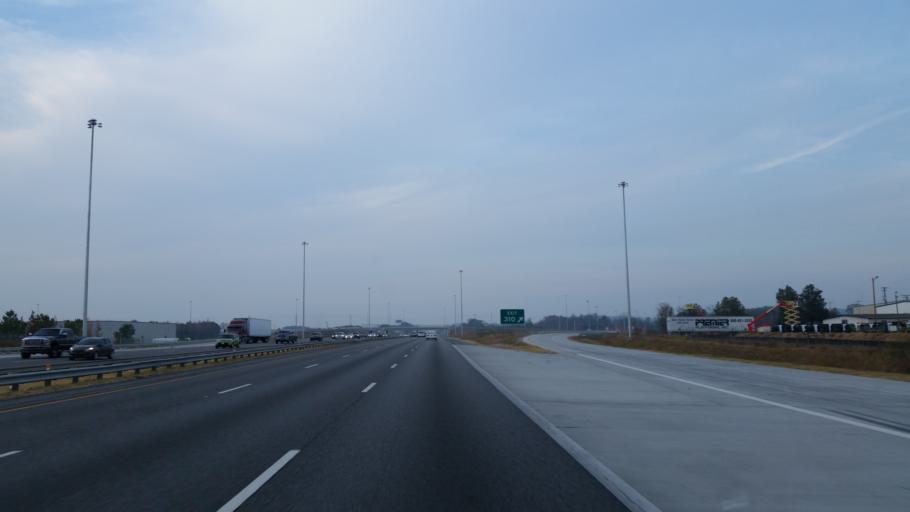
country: US
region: Georgia
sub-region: Bartow County
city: Adairsville
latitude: 34.4360
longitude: -84.9200
